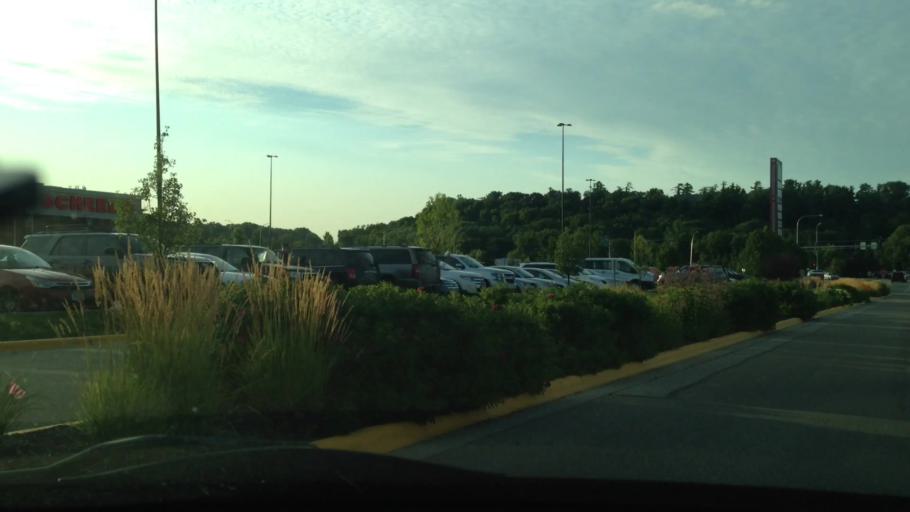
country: US
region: Minnesota
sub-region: Olmsted County
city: Rochester
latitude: 44.0050
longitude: -92.4778
